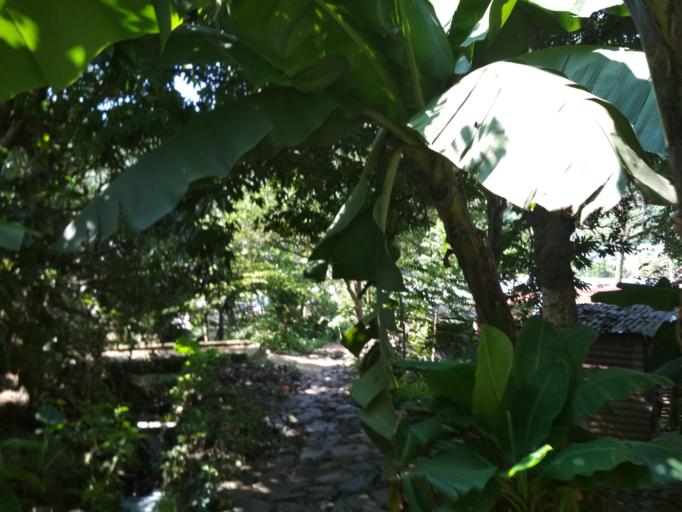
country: MX
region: Veracruz
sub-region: San Andres Tuxtla
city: Texcaltitan Xoteapan (Texcaltitan)
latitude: 18.4483
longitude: -95.2527
